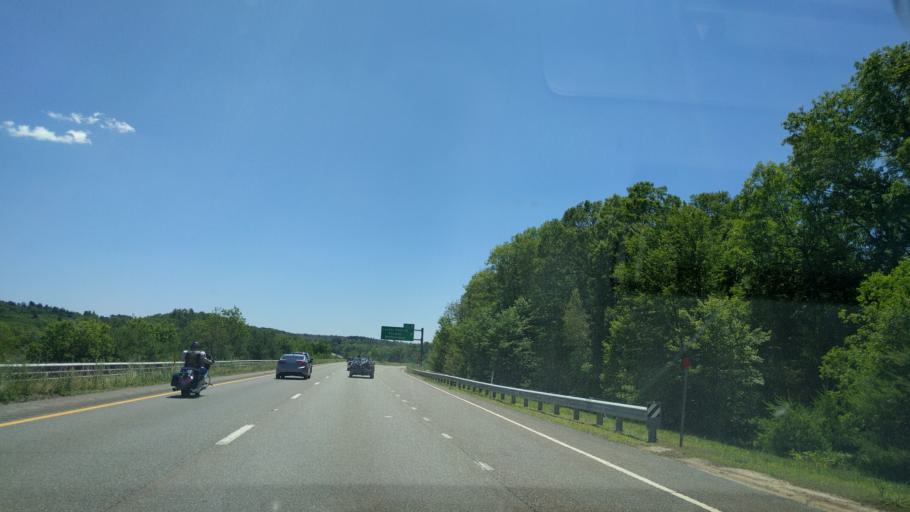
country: US
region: Massachusetts
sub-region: Worcester County
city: East Douglas
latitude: 42.0925
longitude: -71.6979
